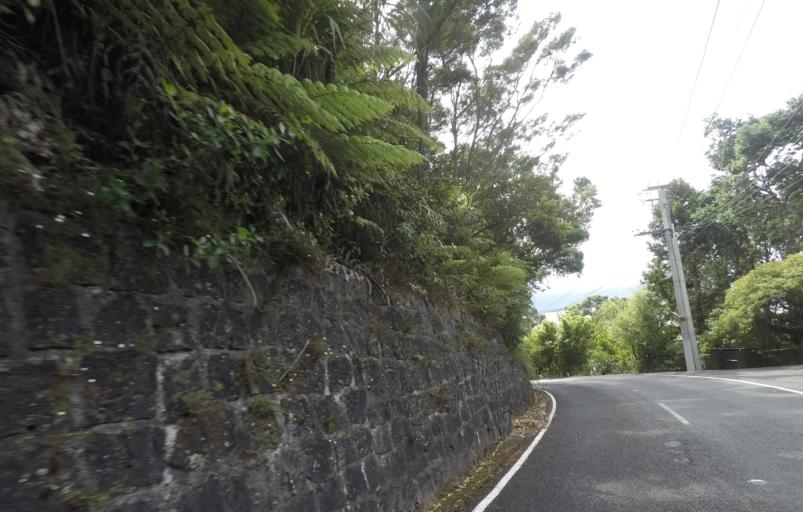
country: NZ
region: Auckland
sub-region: Auckland
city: Titirangi
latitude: -36.9484
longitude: 174.6652
